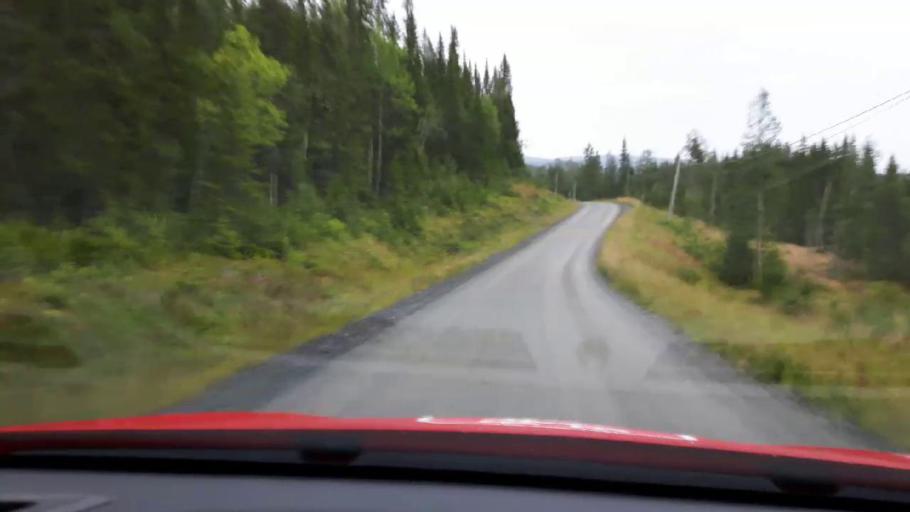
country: SE
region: Jaemtland
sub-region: Are Kommun
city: Are
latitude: 63.5041
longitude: 12.7462
